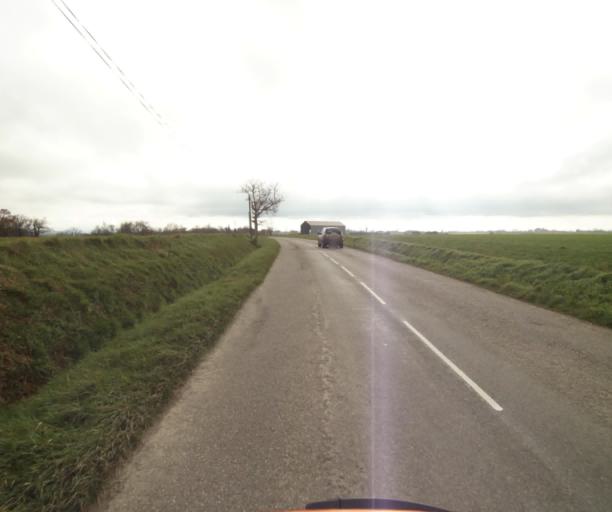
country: FR
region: Languedoc-Roussillon
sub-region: Departement de l'Aude
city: Belpech
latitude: 43.1985
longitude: 1.7328
